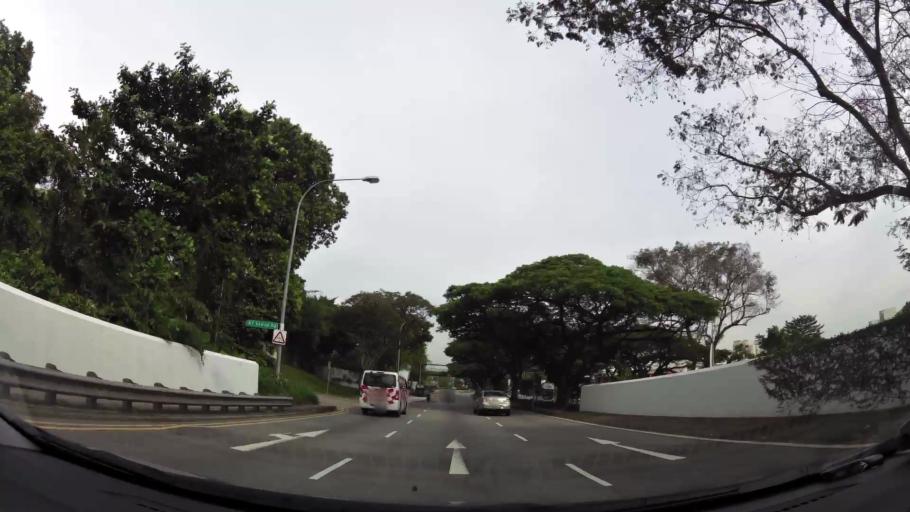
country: SG
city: Singapore
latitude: 1.3183
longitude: 103.7849
